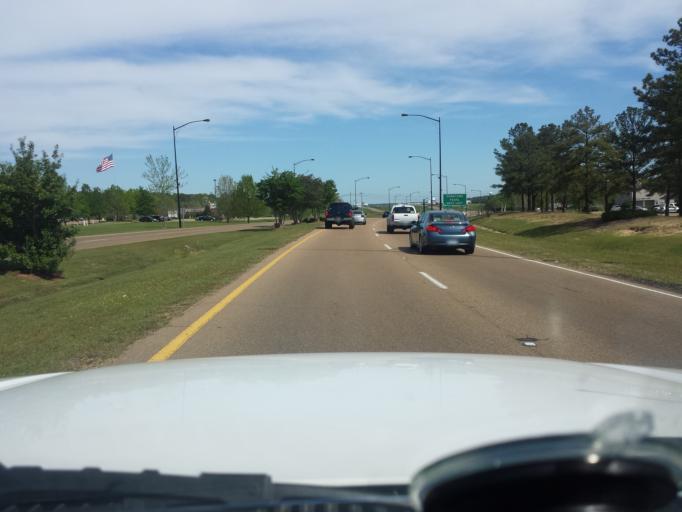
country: US
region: Mississippi
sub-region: Rankin County
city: Pearl
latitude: 32.2803
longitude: -90.0741
